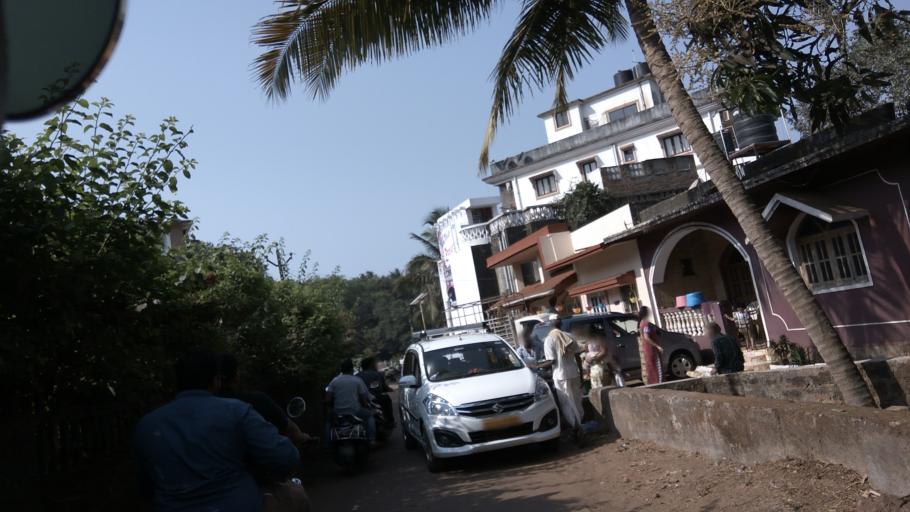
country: IN
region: Goa
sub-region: North Goa
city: Candolim
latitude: 15.5233
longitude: 73.7707
